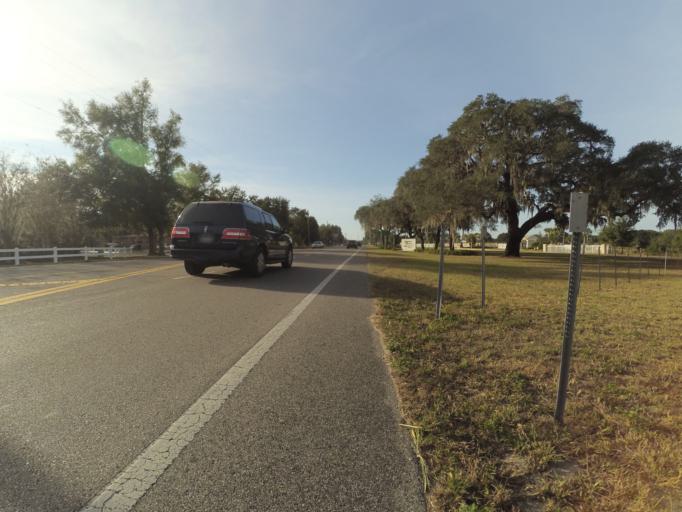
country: US
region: Florida
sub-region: Lake County
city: Umatilla
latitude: 28.9626
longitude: -81.6502
